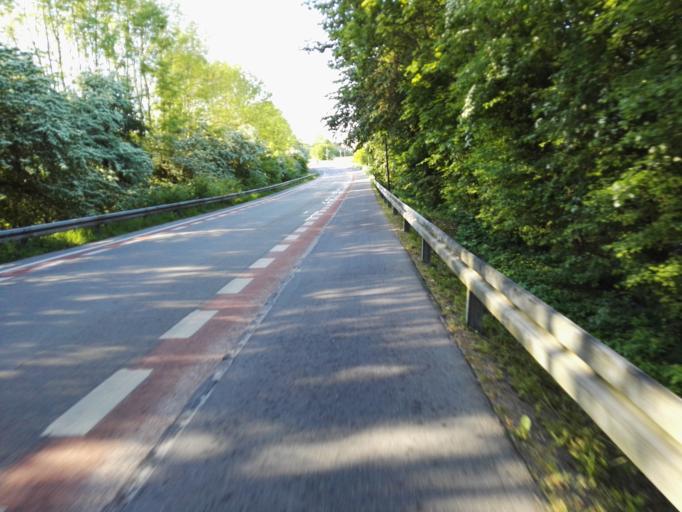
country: DK
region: Capital Region
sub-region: Ballerup Kommune
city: Ballerup
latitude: 55.7422
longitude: 12.3533
